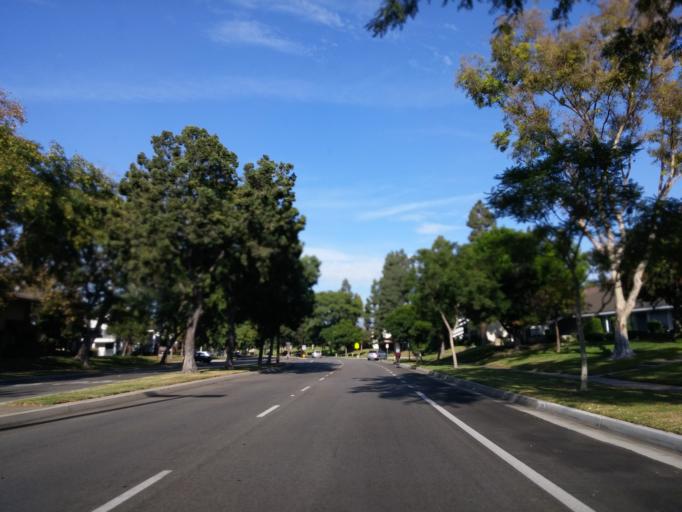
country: US
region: California
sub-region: Orange County
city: Irvine
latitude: 33.6829
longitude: -117.8051
